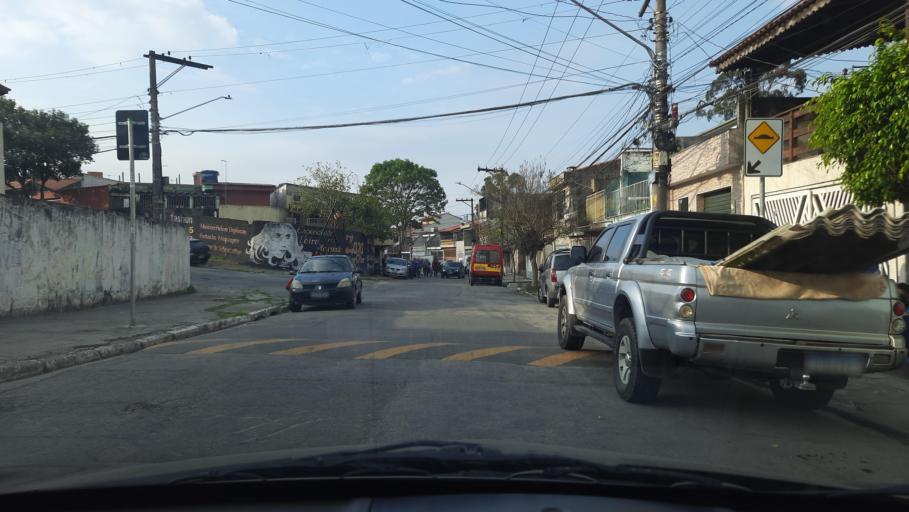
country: BR
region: Sao Paulo
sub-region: Caieiras
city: Caieiras
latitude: -23.4371
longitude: -46.7486
